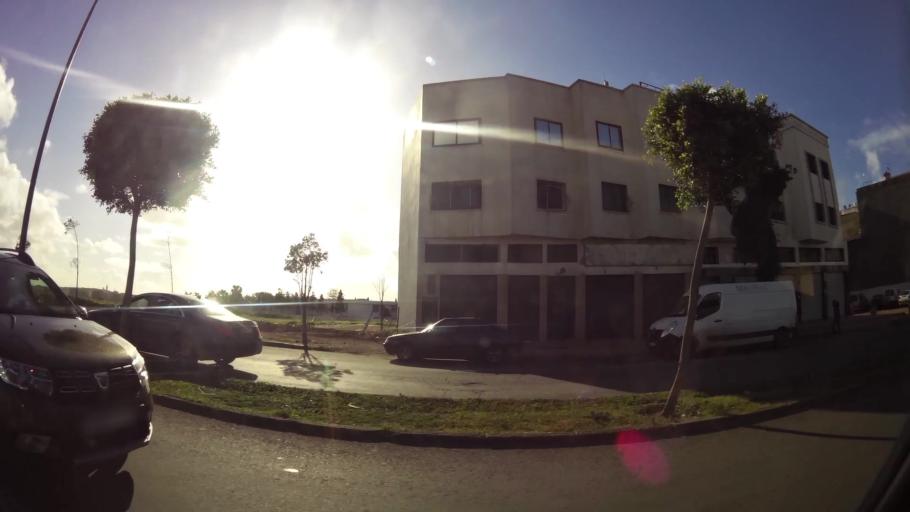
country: MA
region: Grand Casablanca
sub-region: Casablanca
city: Casablanca
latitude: 33.5636
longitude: -7.6833
